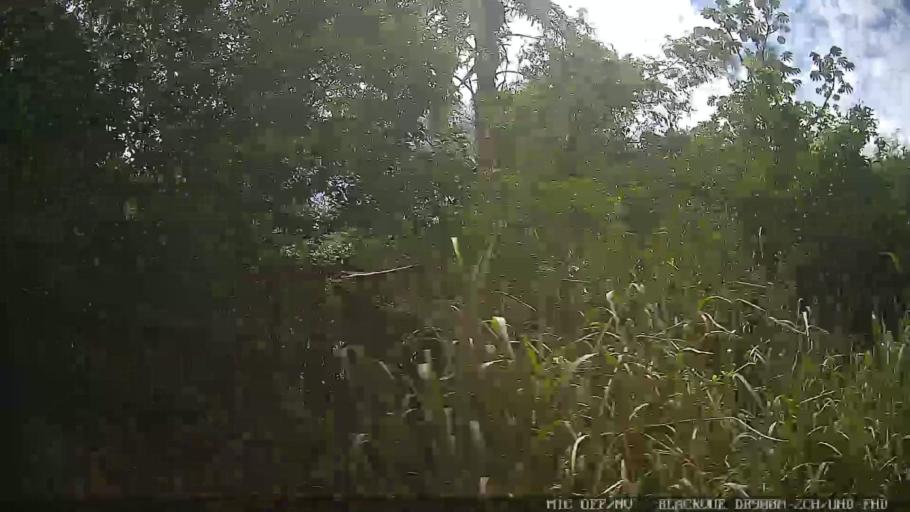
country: BR
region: Sao Paulo
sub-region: Jaguariuna
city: Jaguariuna
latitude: -22.7602
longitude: -47.0060
